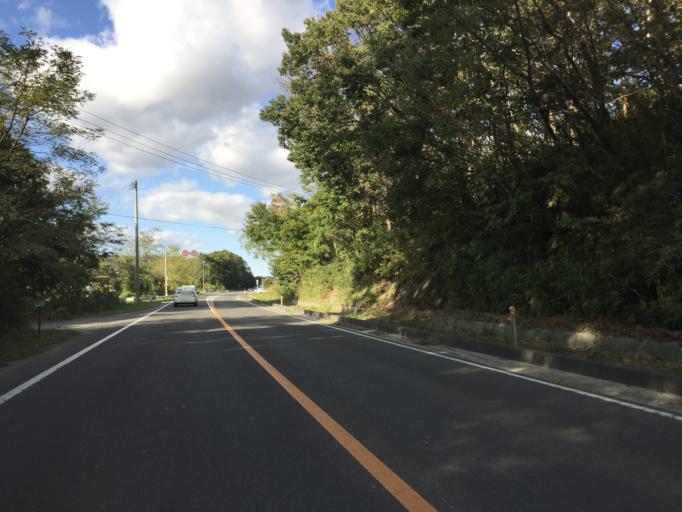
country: JP
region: Miyagi
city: Marumori
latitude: 37.9011
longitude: 140.9004
